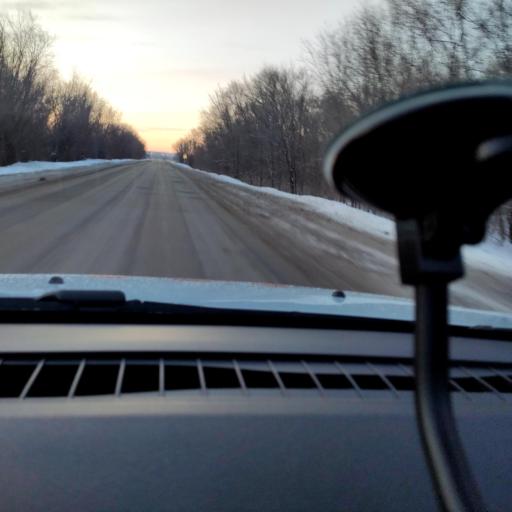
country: RU
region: Samara
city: Samara
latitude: 53.0962
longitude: 50.2298
